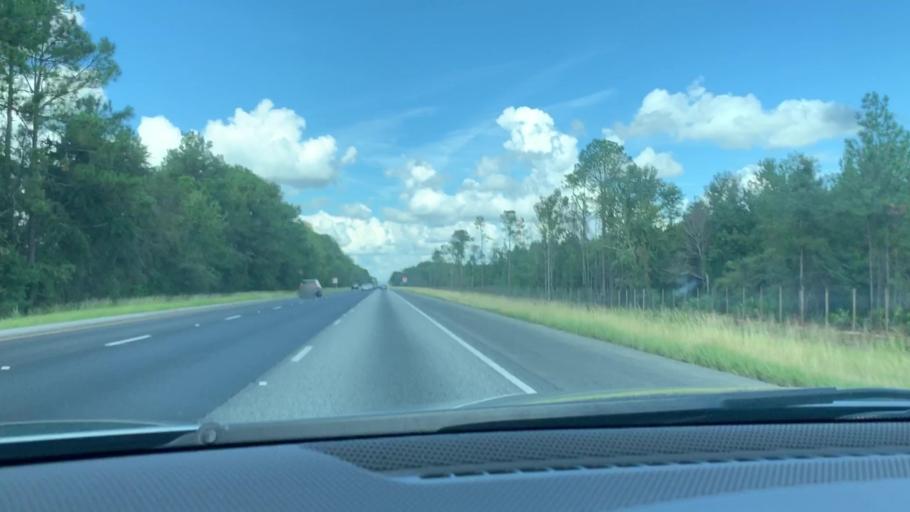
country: US
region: Georgia
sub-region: Camden County
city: Woodbine
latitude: 30.8975
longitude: -81.6857
